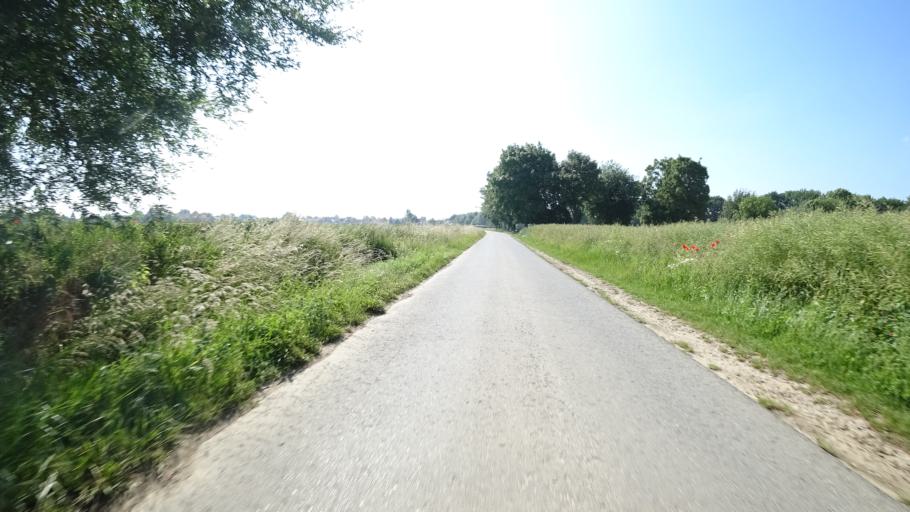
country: DE
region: North Rhine-Westphalia
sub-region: Regierungsbezirk Arnsberg
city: Lippstadt
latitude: 51.6405
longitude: 8.3821
